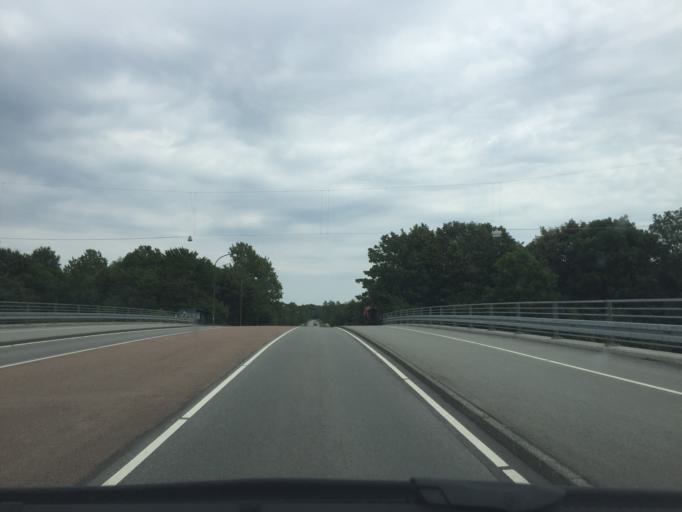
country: DK
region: Capital Region
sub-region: Lyngby-Tarbaek Kommune
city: Kongens Lyngby
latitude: 55.7876
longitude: 12.5283
